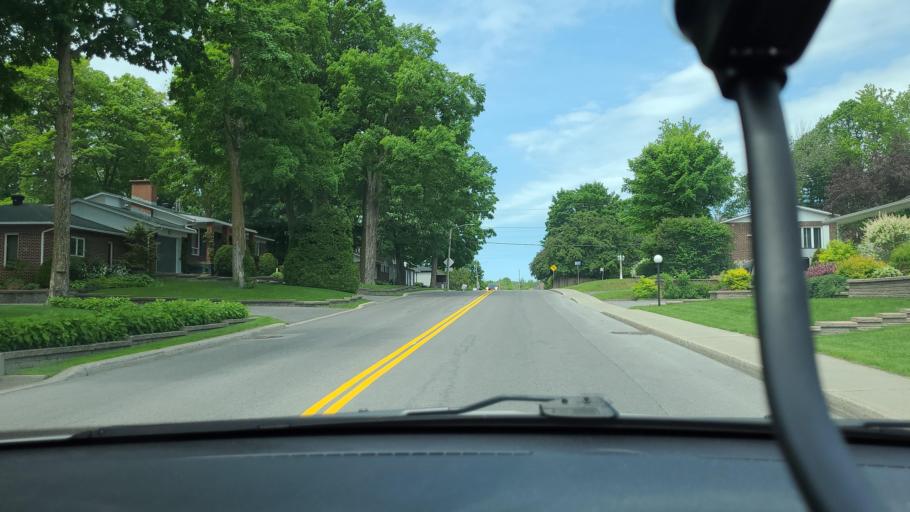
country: CA
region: Quebec
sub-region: Lanaudiere
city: Crabtree
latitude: 45.9685
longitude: -73.4797
